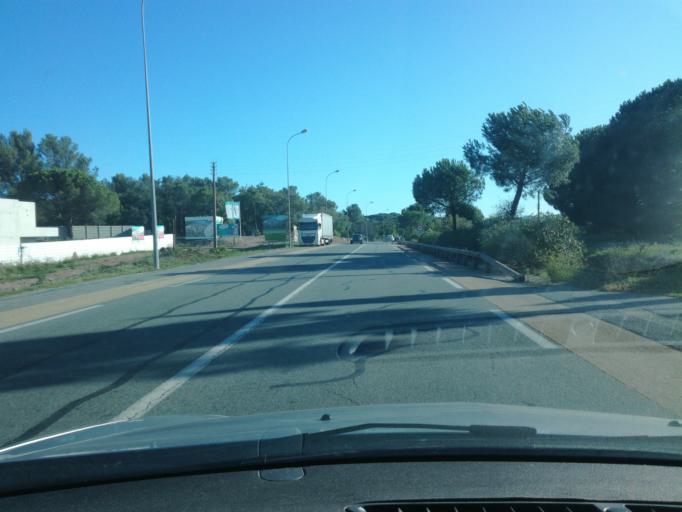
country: FR
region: Provence-Alpes-Cote d'Azur
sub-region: Departement du Var
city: Frejus
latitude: 43.4690
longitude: 6.7445
